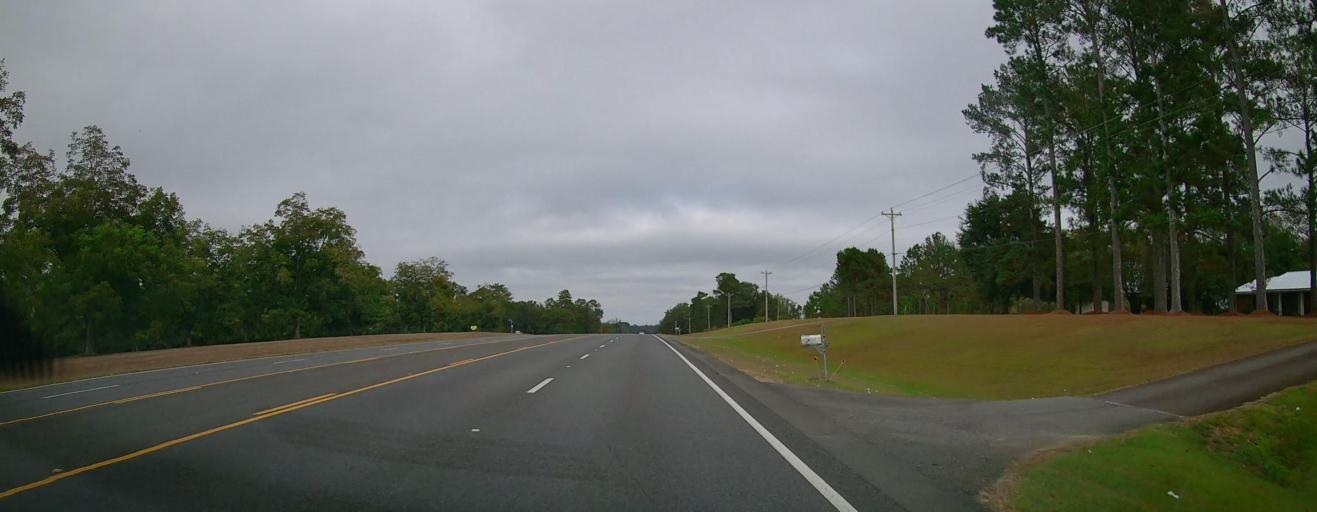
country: US
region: Georgia
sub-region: Thomas County
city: Thomasville
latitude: 30.9544
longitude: -83.8965
